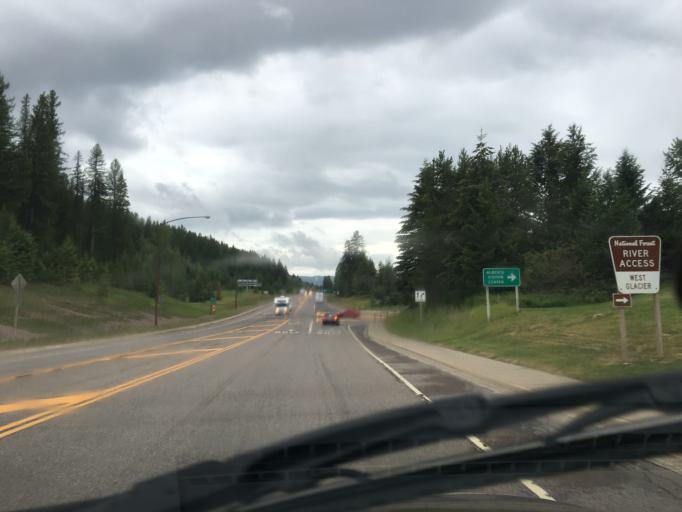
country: US
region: Montana
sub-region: Flathead County
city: Columbia Falls
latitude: 48.4956
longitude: -113.9800
